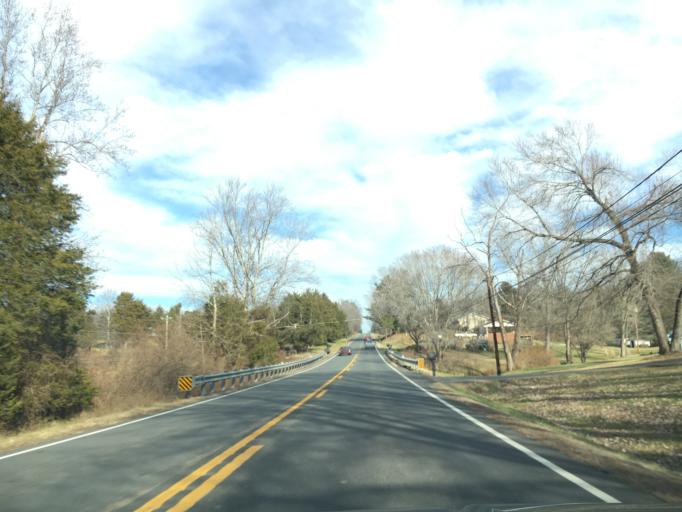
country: US
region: Virginia
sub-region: Culpeper County
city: Culpeper
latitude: 38.6036
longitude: -77.9572
